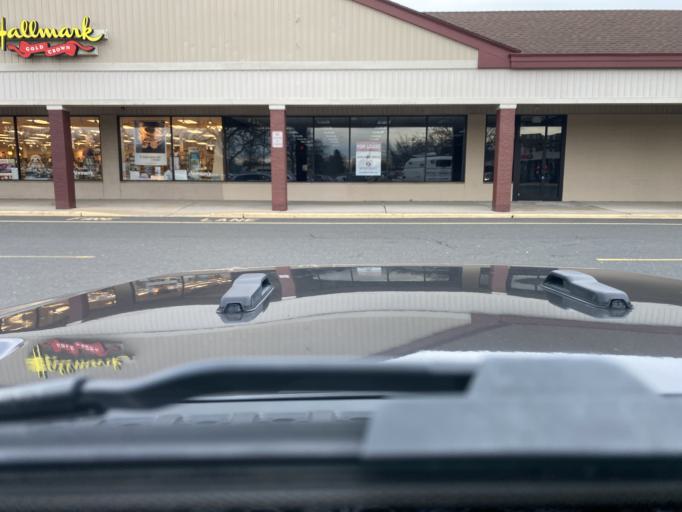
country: US
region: New Jersey
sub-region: Somerset County
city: Bloomingdale
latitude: 40.4999
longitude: -74.6442
